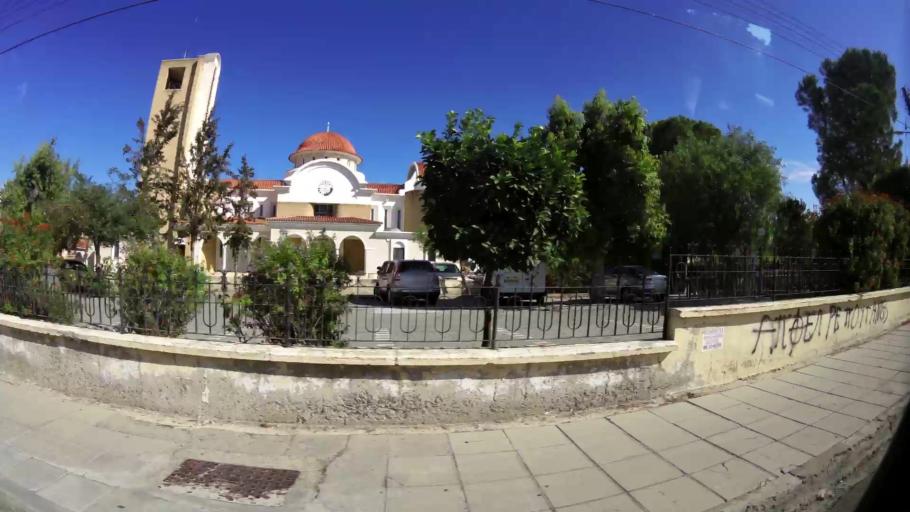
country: CY
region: Lefkosia
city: Nicosia
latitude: 35.1361
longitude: 33.3382
